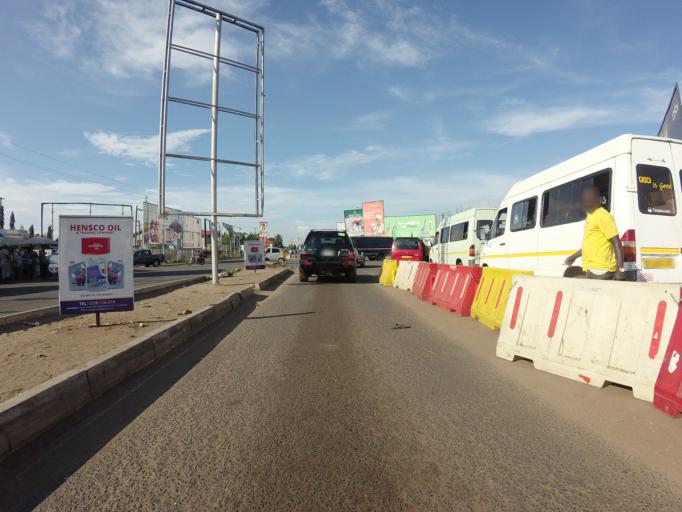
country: GH
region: Greater Accra
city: Nungua
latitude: 5.6138
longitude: -0.0739
